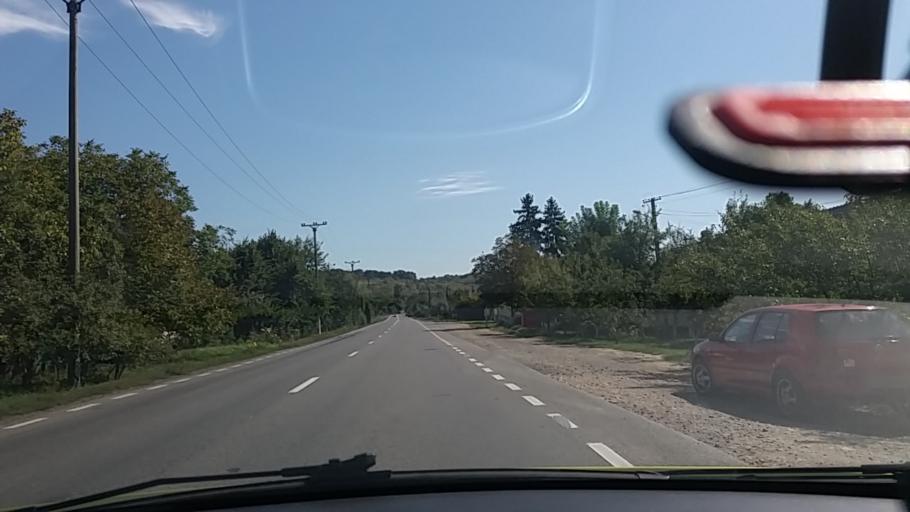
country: RO
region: Arad
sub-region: Comuna Zabrani
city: Neudorf
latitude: 46.1069
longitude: 21.6300
